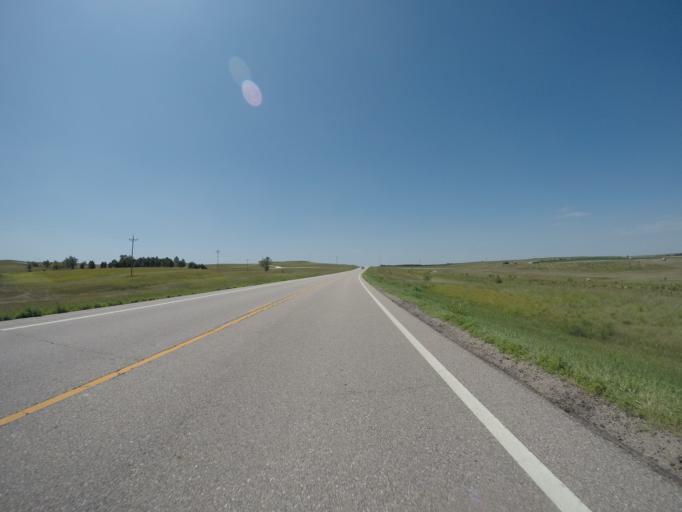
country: US
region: Kansas
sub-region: Osborne County
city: Osborne
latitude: 39.4986
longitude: -98.6939
